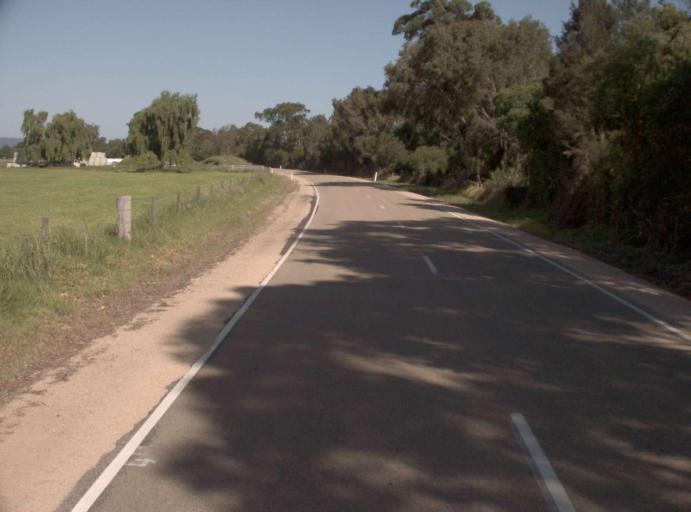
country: AU
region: Victoria
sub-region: East Gippsland
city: Lakes Entrance
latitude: -37.7205
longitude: 148.4754
